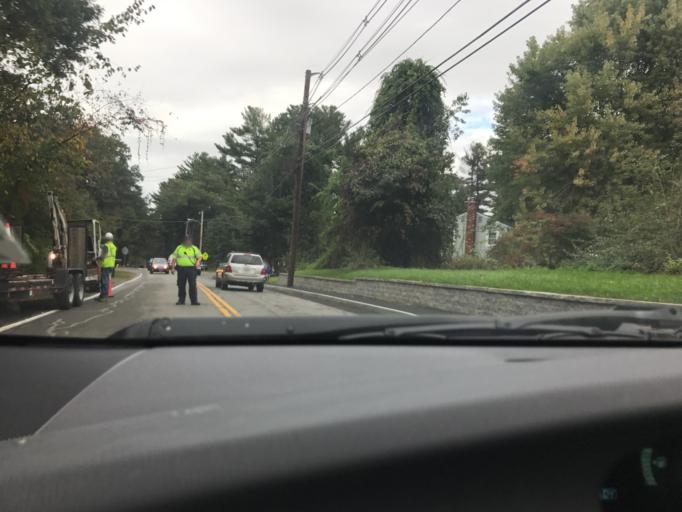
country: US
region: Massachusetts
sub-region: Middlesex County
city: Littleton Common
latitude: 42.5681
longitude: -71.4639
